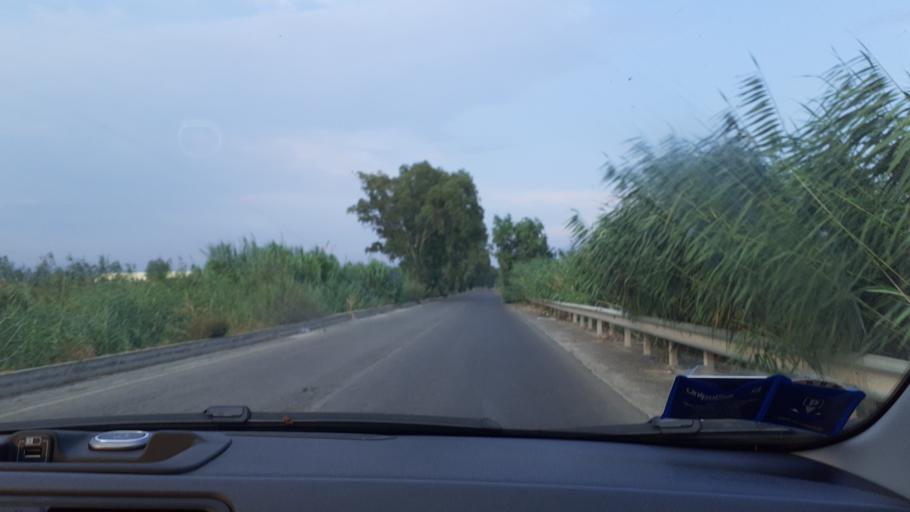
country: IT
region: Sicily
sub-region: Catania
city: Misterbianco
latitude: 37.4397
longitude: 15.0084
